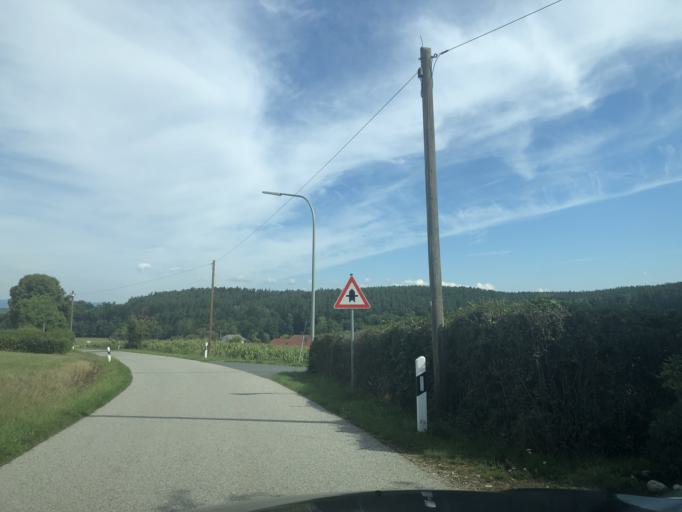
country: DE
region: Bavaria
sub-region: Upper Palatinate
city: Trabitz
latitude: 49.7855
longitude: 11.8941
